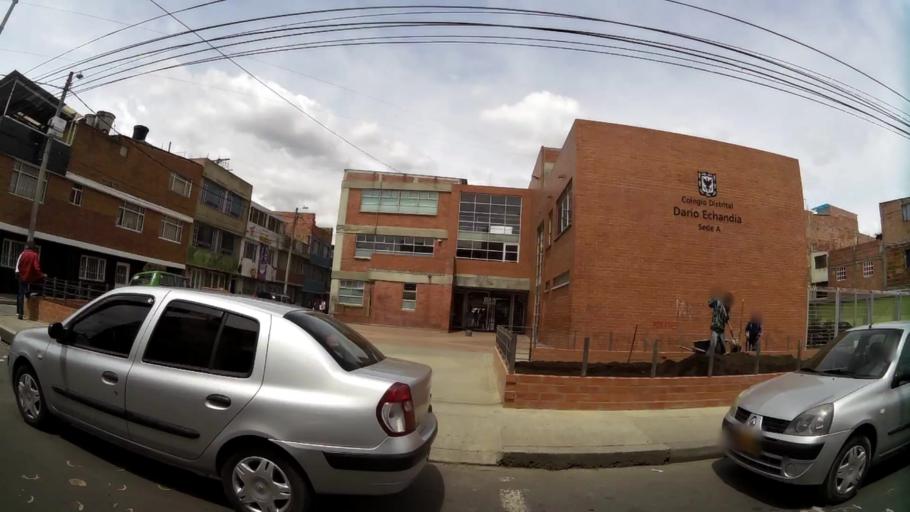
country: CO
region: Cundinamarca
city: Soacha
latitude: 4.6419
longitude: -74.1622
